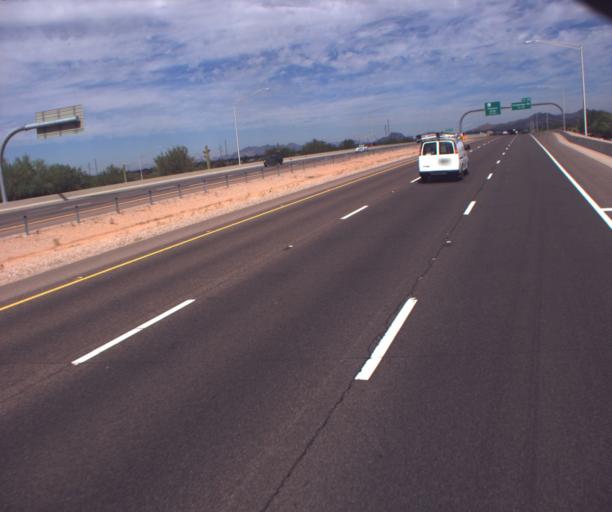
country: US
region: Arizona
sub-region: Maricopa County
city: Queen Creek
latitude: 33.3480
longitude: -111.6437
